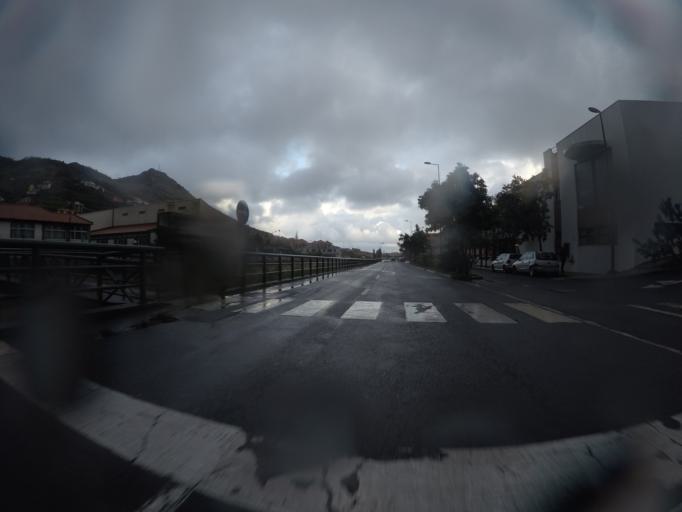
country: PT
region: Madeira
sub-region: Machico
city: Machico
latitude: 32.7251
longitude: -16.7716
